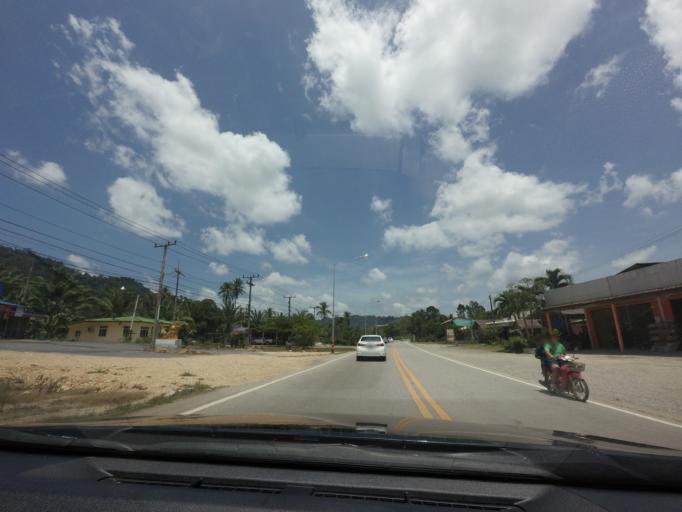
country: TH
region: Chumphon
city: Ban Nam Yuen
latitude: 9.9119
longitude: 98.9169
